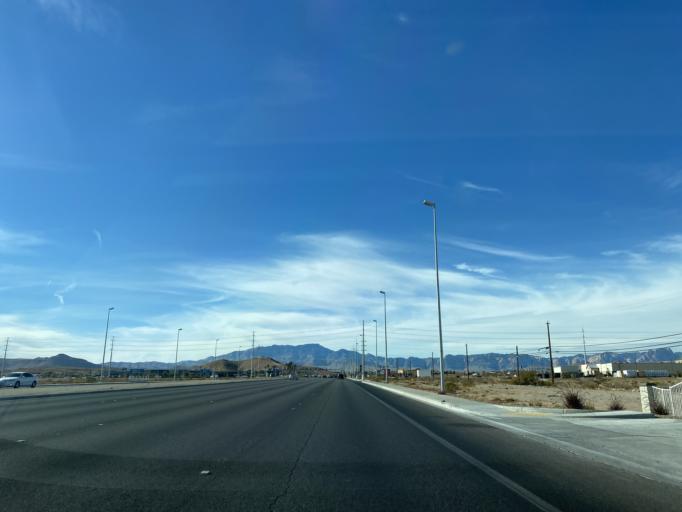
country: US
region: Nevada
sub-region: Clark County
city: Enterprise
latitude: 36.0234
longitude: -115.2386
